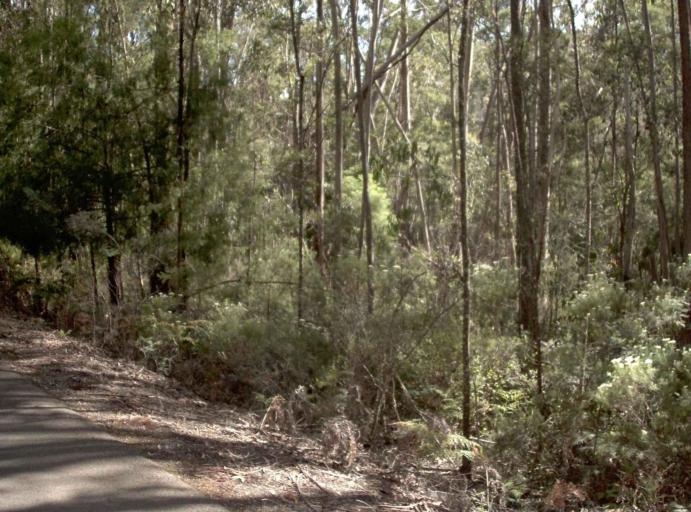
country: AU
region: Victoria
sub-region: East Gippsland
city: Lakes Entrance
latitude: -37.4326
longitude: 148.1288
